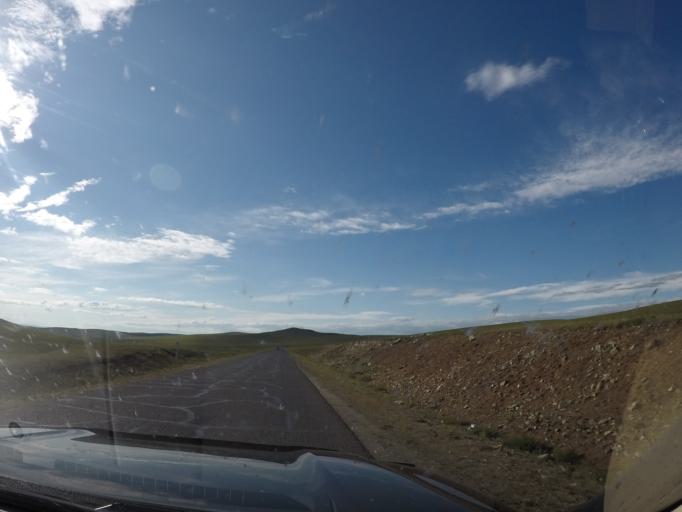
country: MN
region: Hentiy
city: Modot
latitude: 47.8031
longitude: 108.7403
